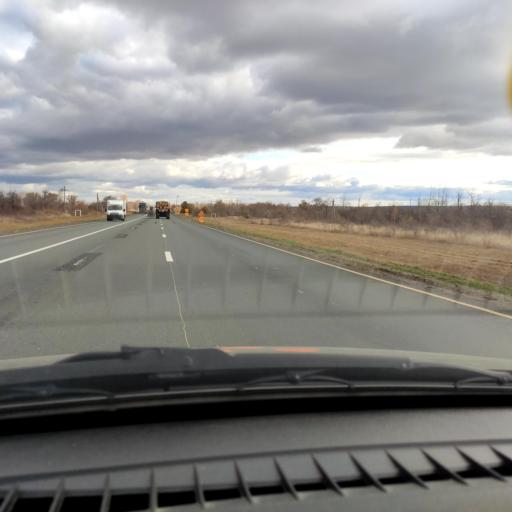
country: RU
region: Samara
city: Syzran'
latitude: 53.2107
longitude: 48.5330
